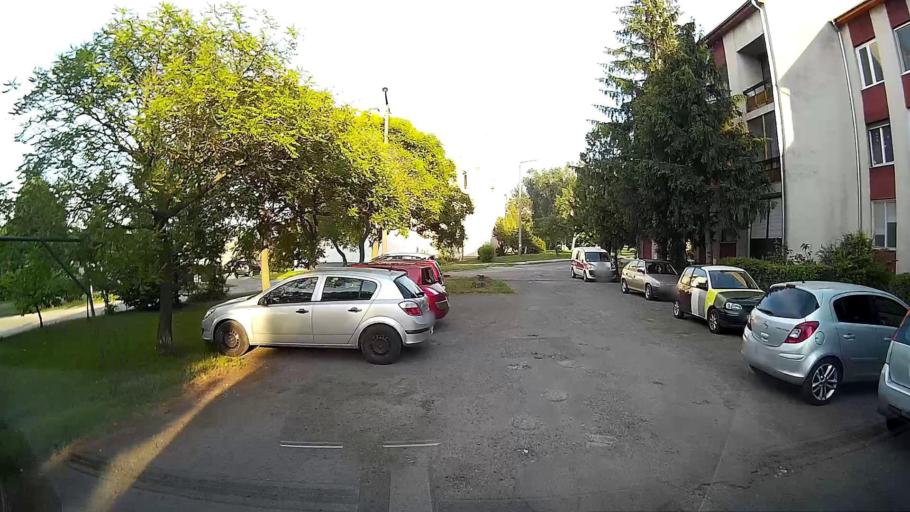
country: HU
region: Pest
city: Szentendre
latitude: 47.6779
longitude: 19.0630
